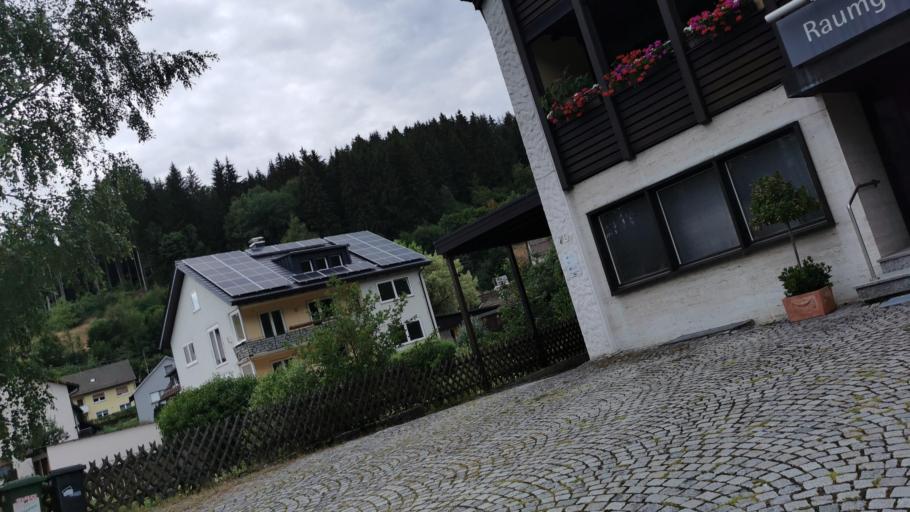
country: DE
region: Bavaria
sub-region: Upper Franconia
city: Steinwiesen
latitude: 50.2978
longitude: 11.4654
